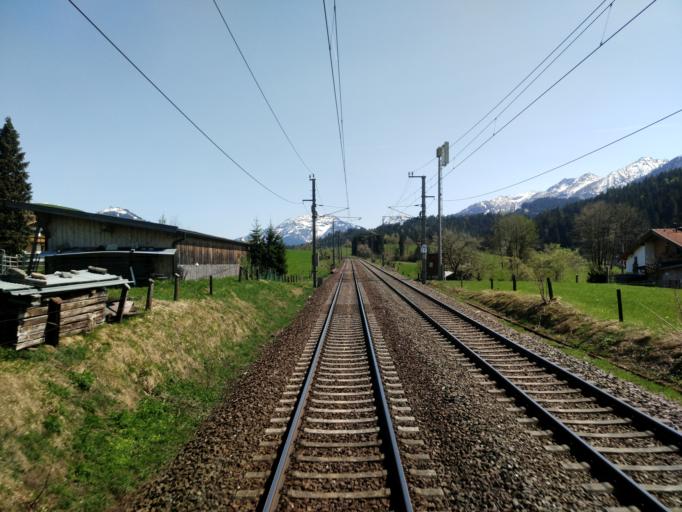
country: AT
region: Tyrol
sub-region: Politischer Bezirk Kitzbuhel
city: Fieberbrunn
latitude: 47.5014
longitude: 12.4888
